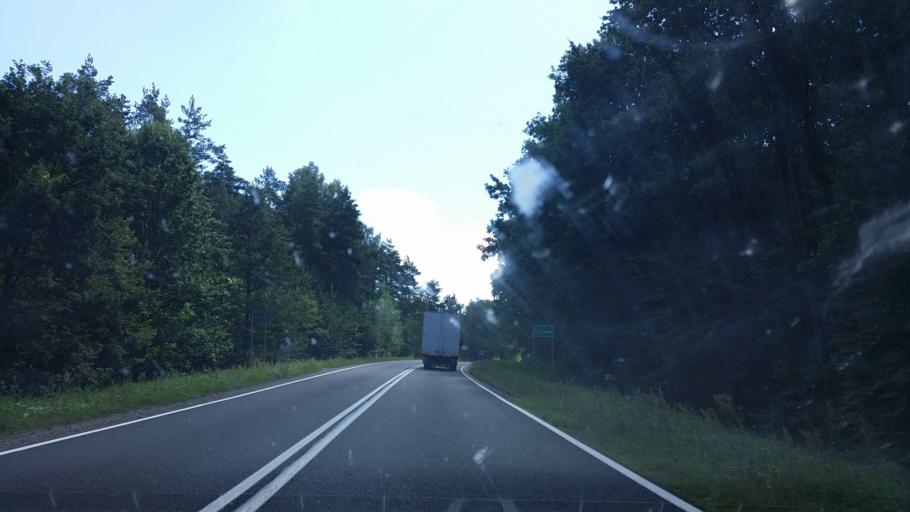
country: PL
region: West Pomeranian Voivodeship
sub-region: Powiat drawski
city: Kalisz Pomorski
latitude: 53.2953
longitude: 15.8504
